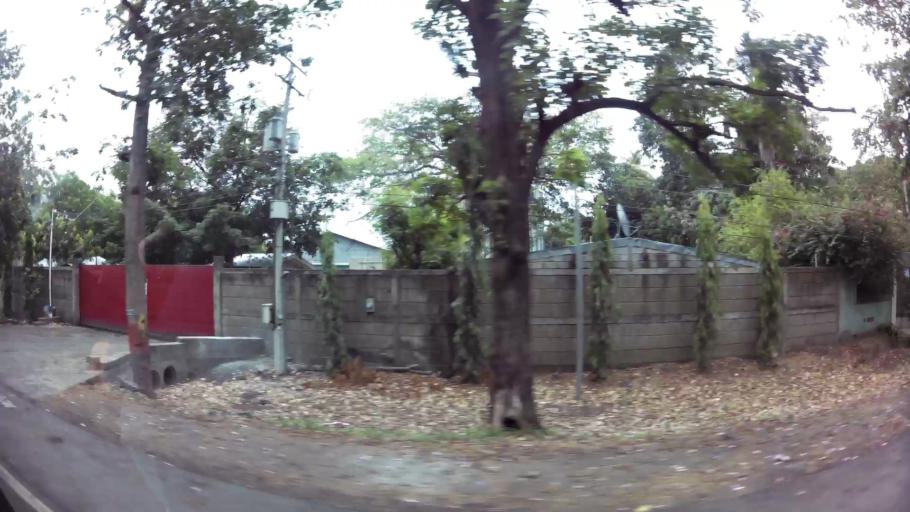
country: NI
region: Chinandega
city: Chinandega
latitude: 12.6170
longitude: -87.1047
